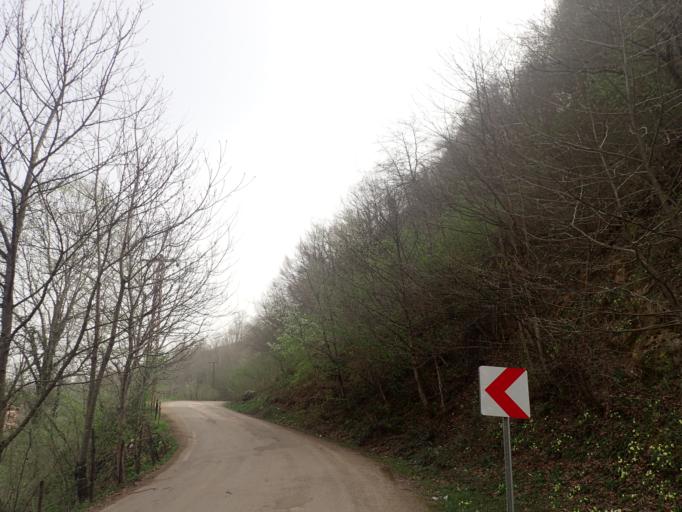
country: TR
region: Ordu
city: Kumru
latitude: 40.8294
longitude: 37.2800
